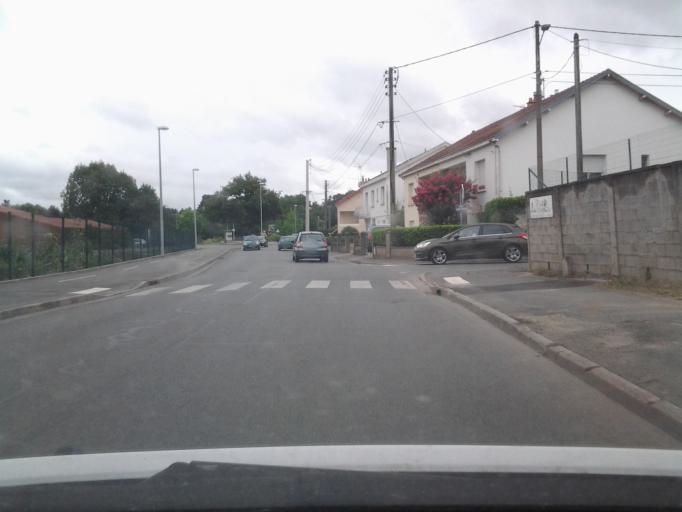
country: FR
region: Pays de la Loire
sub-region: Departement de la Vendee
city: La Roche-sur-Yon
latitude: 46.6628
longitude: -1.4256
